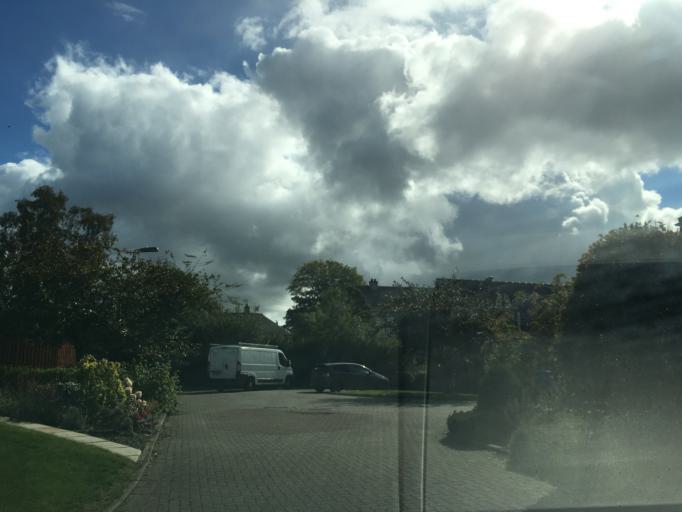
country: GB
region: Scotland
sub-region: Edinburgh
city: Colinton
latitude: 55.9070
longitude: -3.2108
